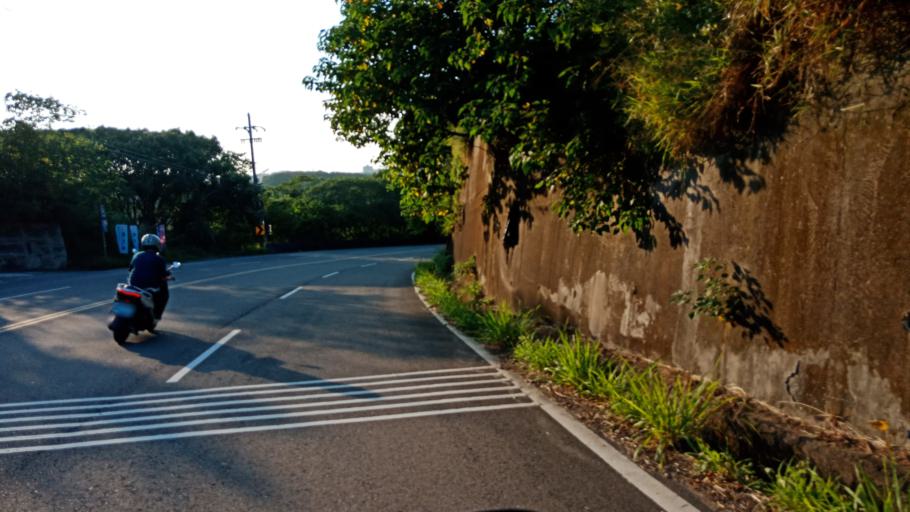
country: TW
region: Taiwan
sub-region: Hsinchu
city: Hsinchu
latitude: 24.7606
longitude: 120.9966
